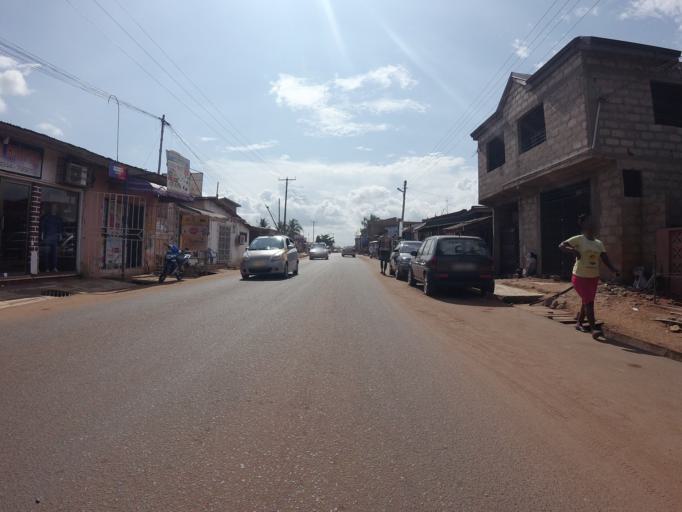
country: GH
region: Greater Accra
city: Medina Estates
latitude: 5.6789
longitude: -0.1787
